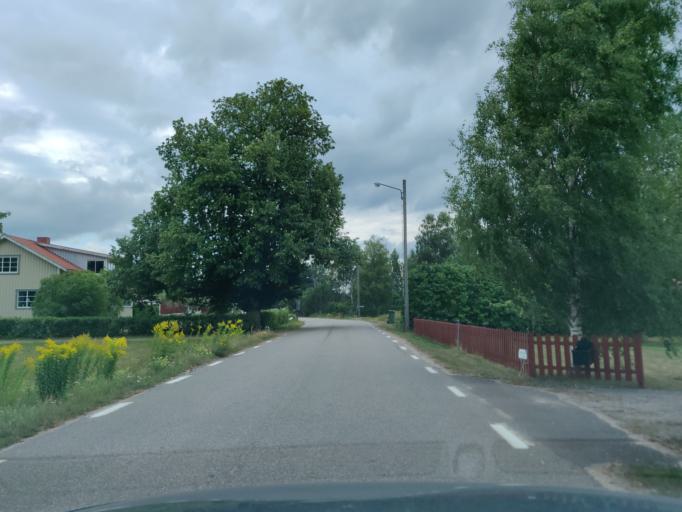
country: SE
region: Vaermland
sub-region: Munkfors Kommun
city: Munkfors
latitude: 59.8770
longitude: 13.5589
